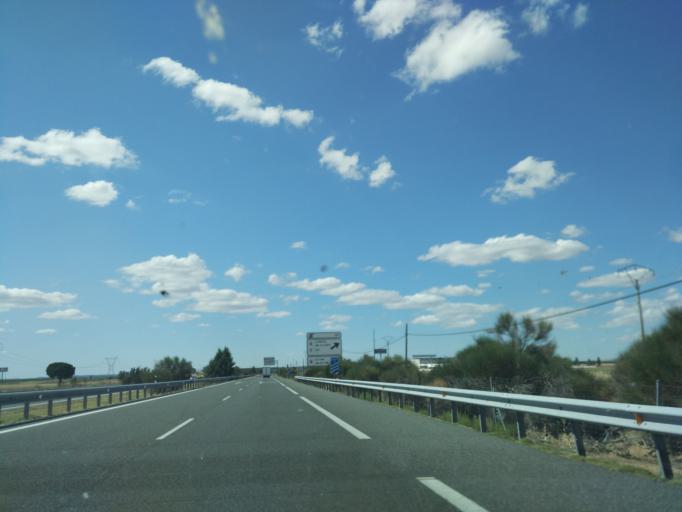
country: ES
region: Castille and Leon
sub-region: Provincia de Valladolid
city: San Vicente del Palacio
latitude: 41.2168
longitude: -4.8388
